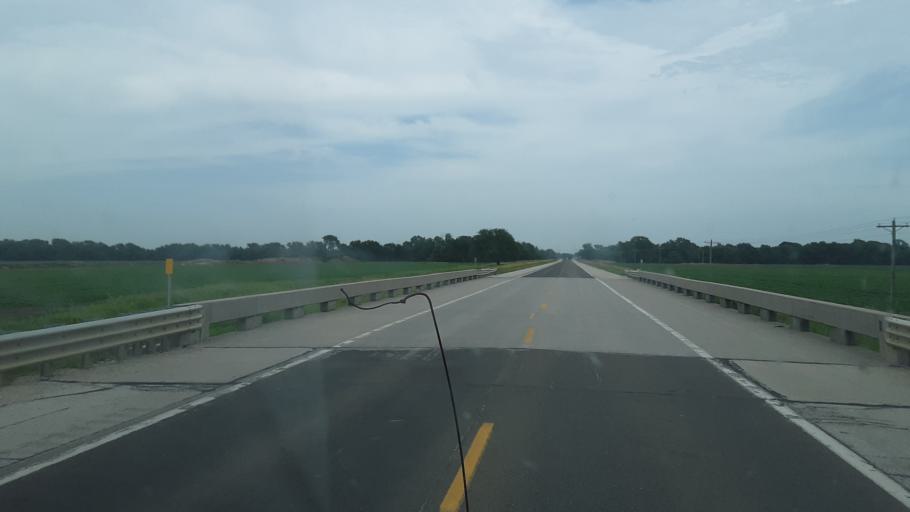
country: US
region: Kansas
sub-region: Allen County
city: Iola
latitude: 37.9219
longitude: -95.4358
